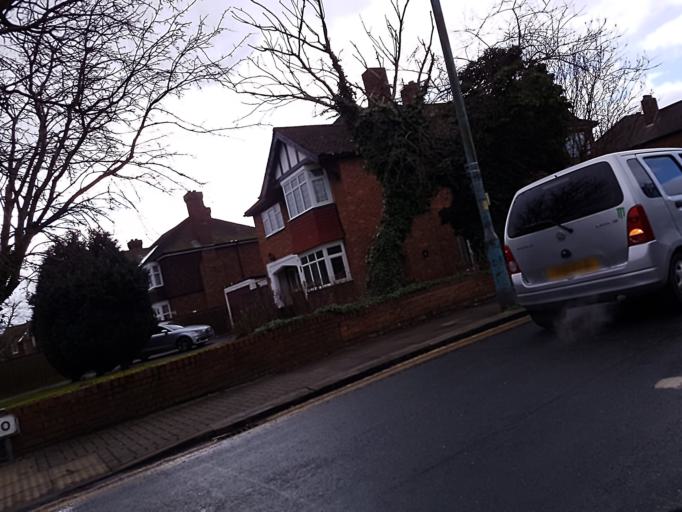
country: GB
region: England
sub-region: North East Lincolnshire
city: Grimbsy
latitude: 53.5566
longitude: -0.0916
